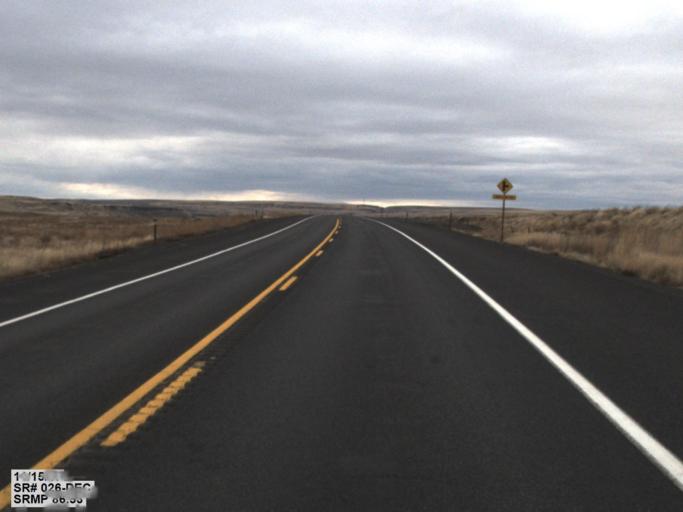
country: US
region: Washington
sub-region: Adams County
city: Ritzville
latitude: 46.7452
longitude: -118.2387
